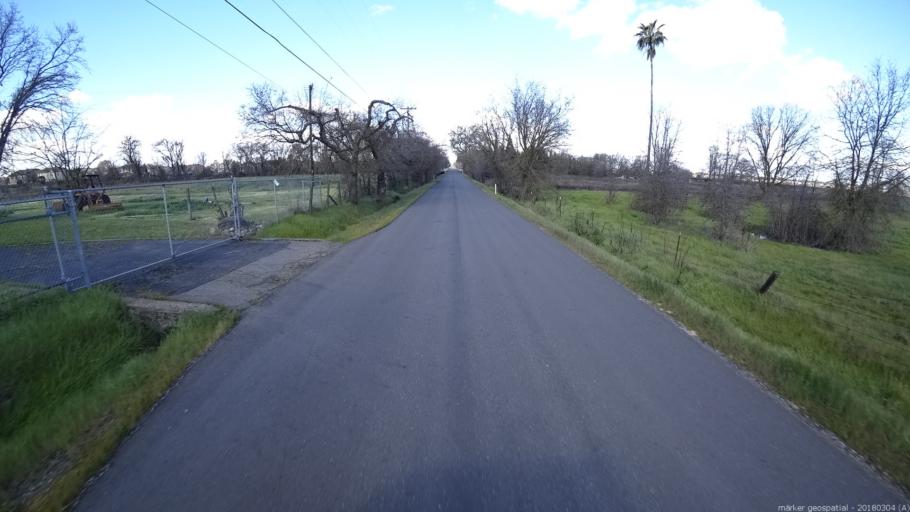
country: US
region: California
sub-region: Sacramento County
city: Vineyard
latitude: 38.4624
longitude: -121.3301
